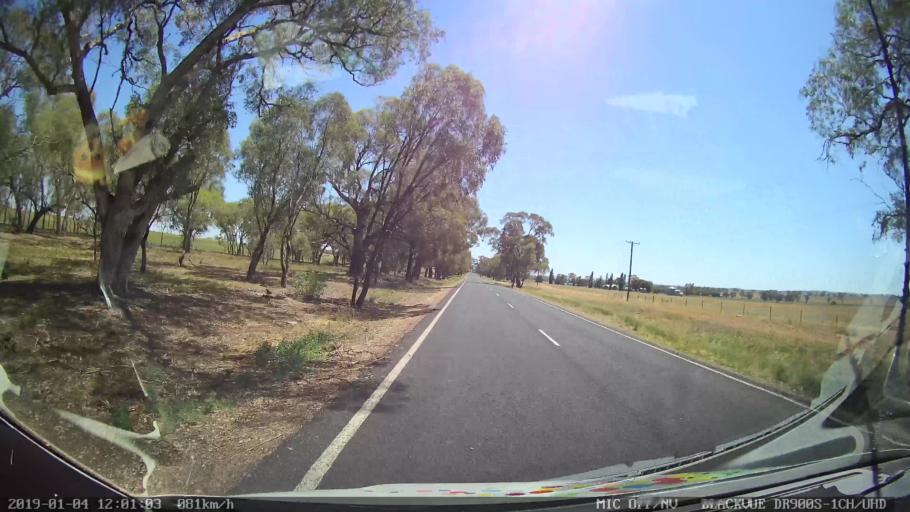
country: AU
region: New South Wales
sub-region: Cabonne
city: Molong
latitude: -32.7956
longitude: 148.6895
